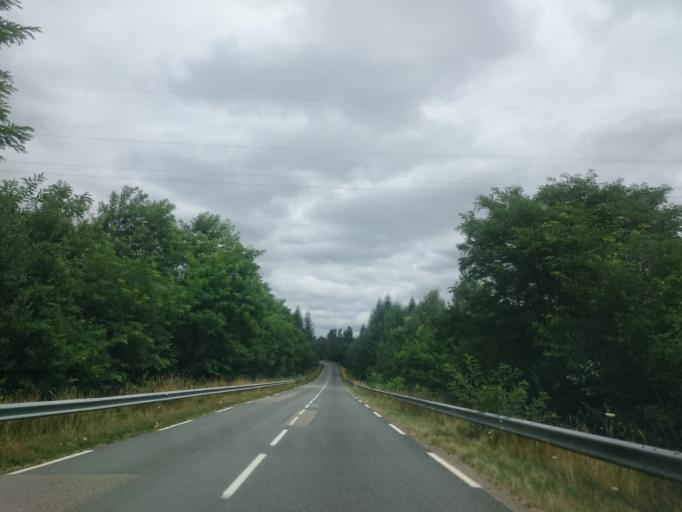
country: FR
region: Auvergne
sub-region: Departement du Cantal
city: Laroquebrou
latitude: 44.9695
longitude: 2.2151
